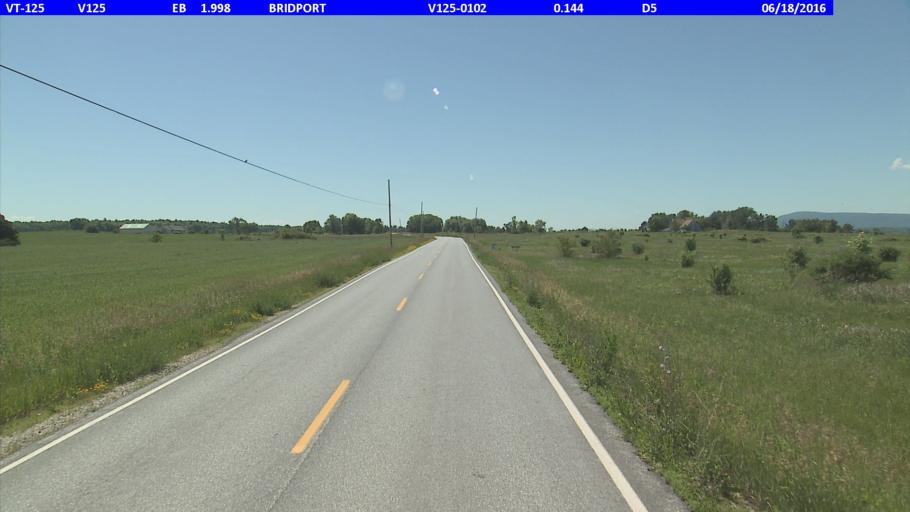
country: US
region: New York
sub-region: Essex County
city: Port Henry
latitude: 44.0200
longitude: -73.3904
